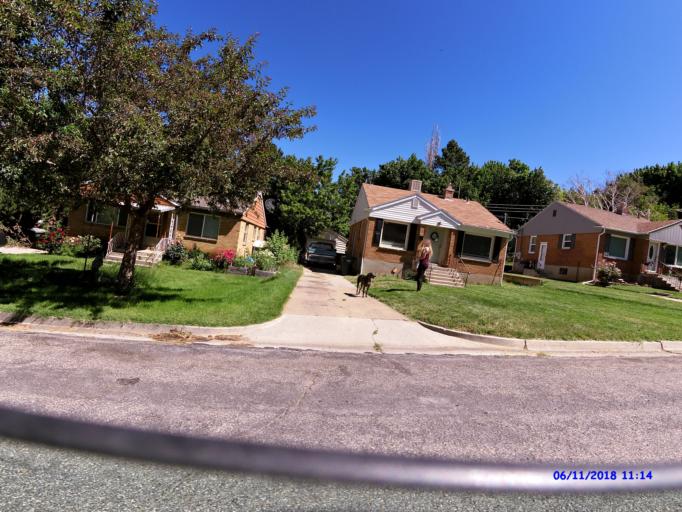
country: US
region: Utah
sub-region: Weber County
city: Ogden
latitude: 41.2212
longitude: -111.9335
